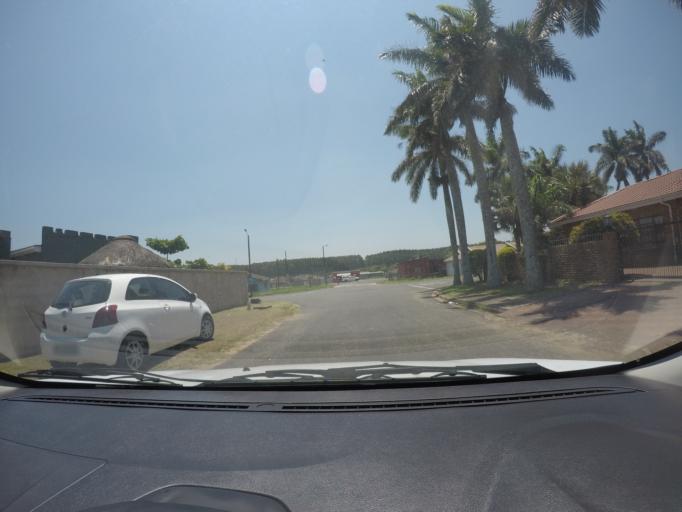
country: ZA
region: KwaZulu-Natal
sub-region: uThungulu District Municipality
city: eSikhawini
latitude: -28.8883
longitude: 31.8837
